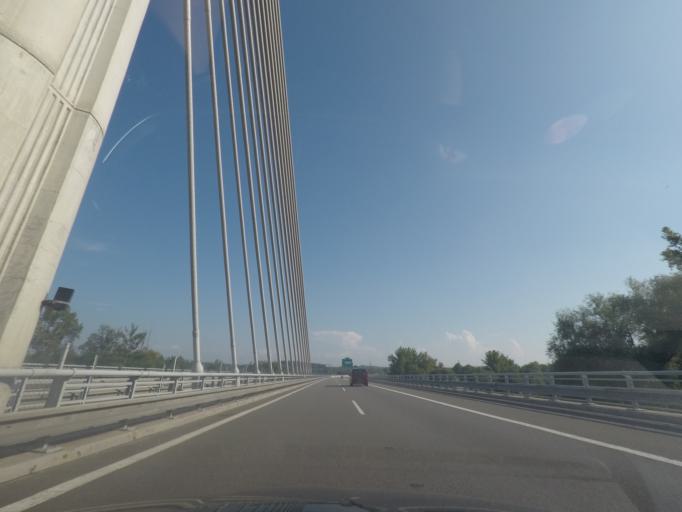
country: PL
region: Silesian Voivodeship
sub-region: Powiat raciborski
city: Chalupki
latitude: 49.8877
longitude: 18.3050
